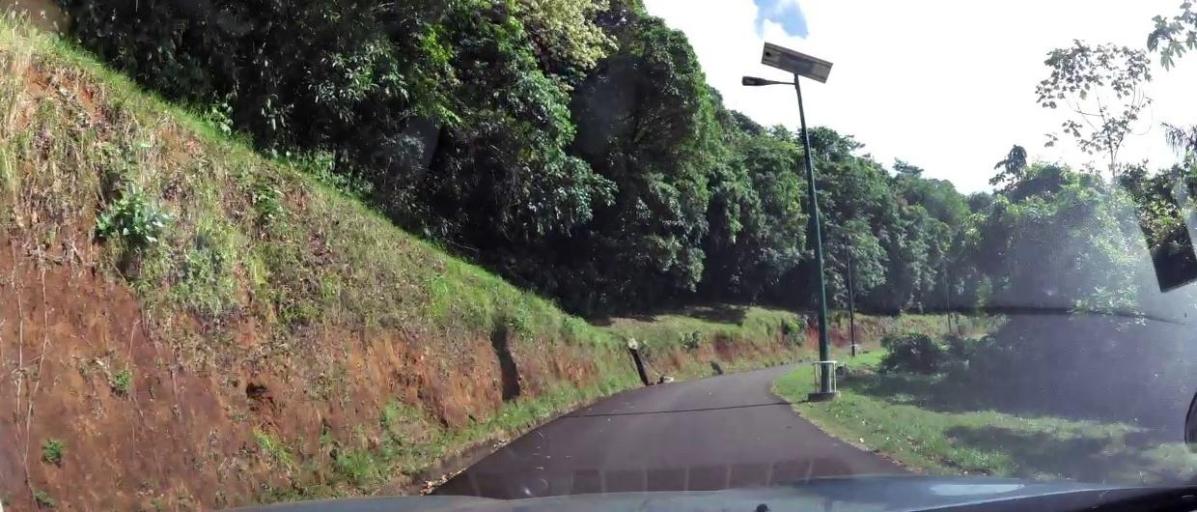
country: GF
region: Guyane
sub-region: Guyane
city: Cayenne
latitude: 4.9474
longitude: -52.3114
